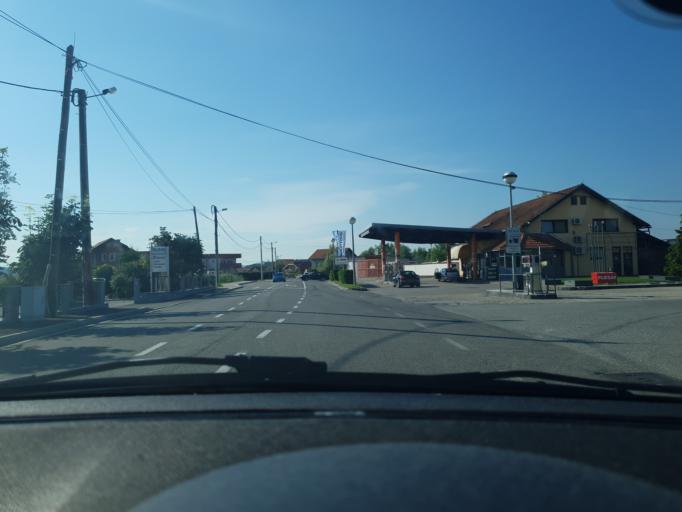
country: HR
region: Zagrebacka
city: Jablanovec
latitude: 45.8977
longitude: 15.8572
